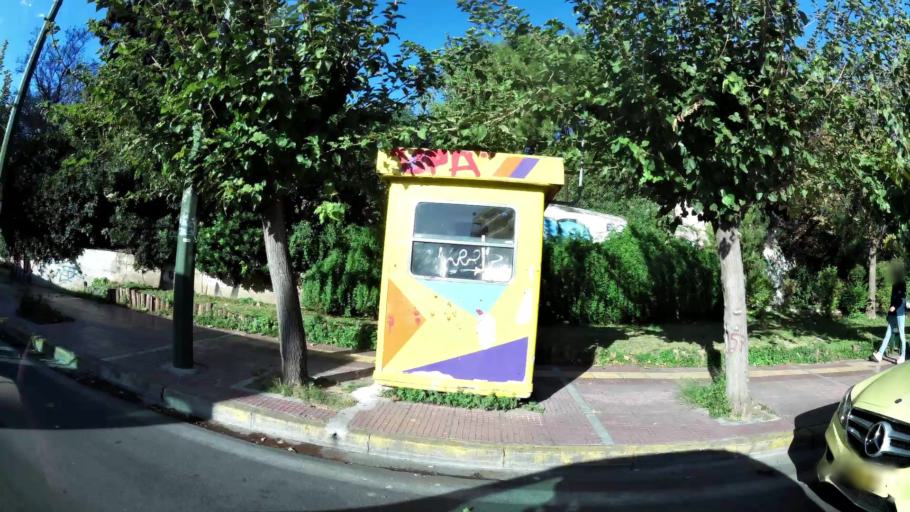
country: GR
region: Attica
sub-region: Nomarchia Athinas
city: Psychiko
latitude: 37.9962
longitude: 23.7681
